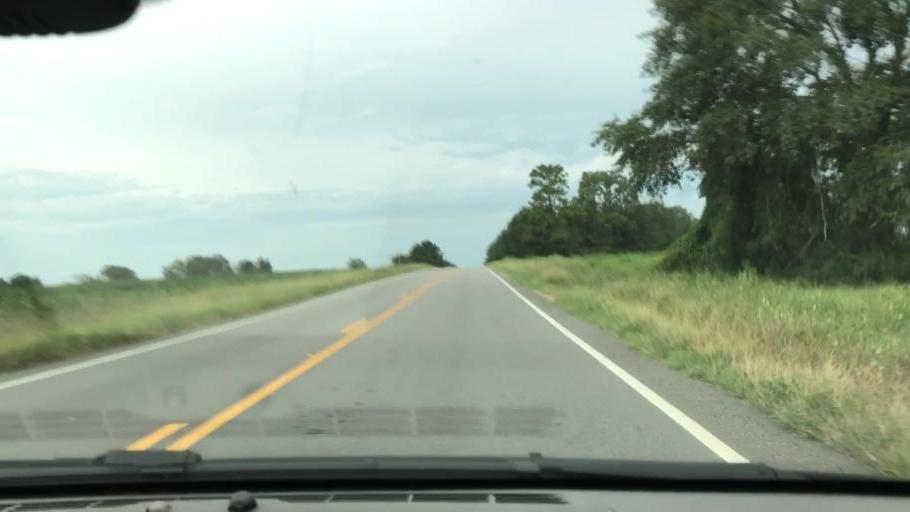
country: US
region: Alabama
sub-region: Houston County
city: Webb
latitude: 31.2796
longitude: -85.1447
